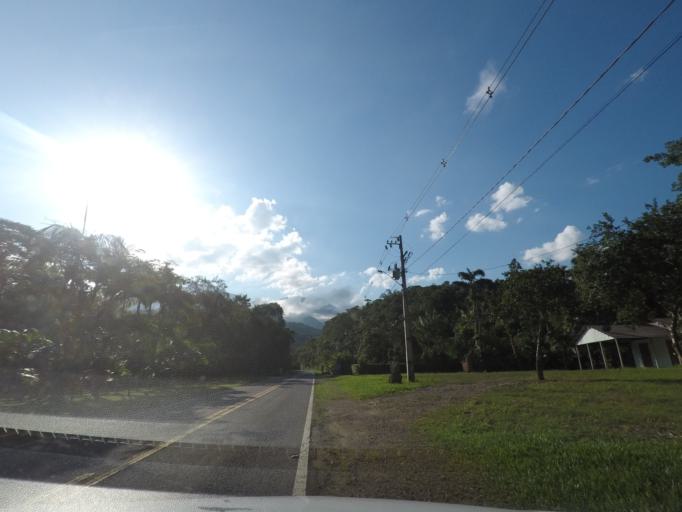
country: BR
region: Parana
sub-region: Antonina
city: Antonina
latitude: -25.4077
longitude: -48.8746
